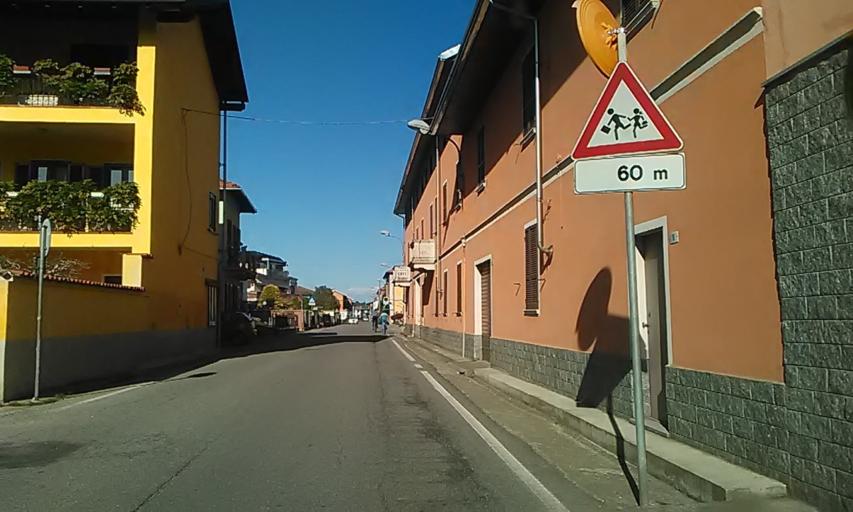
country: IT
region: Piedmont
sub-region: Provincia di Novara
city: Cavaglio D'Agogna
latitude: 45.6107
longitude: 8.4847
